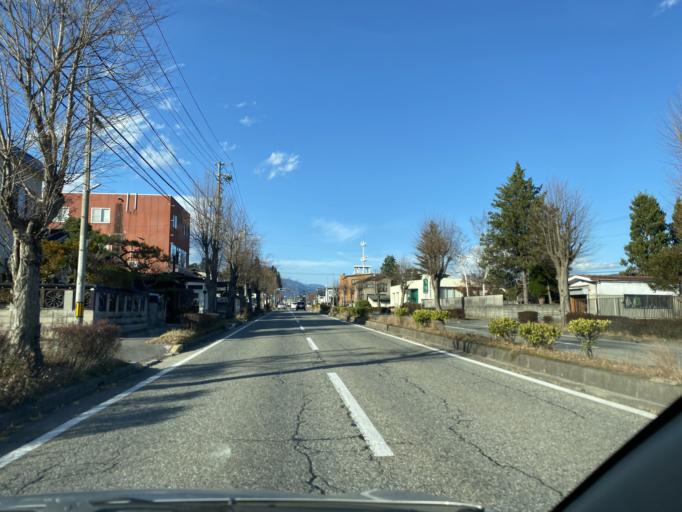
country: JP
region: Nagano
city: Omachi
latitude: 36.5039
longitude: 137.8551
